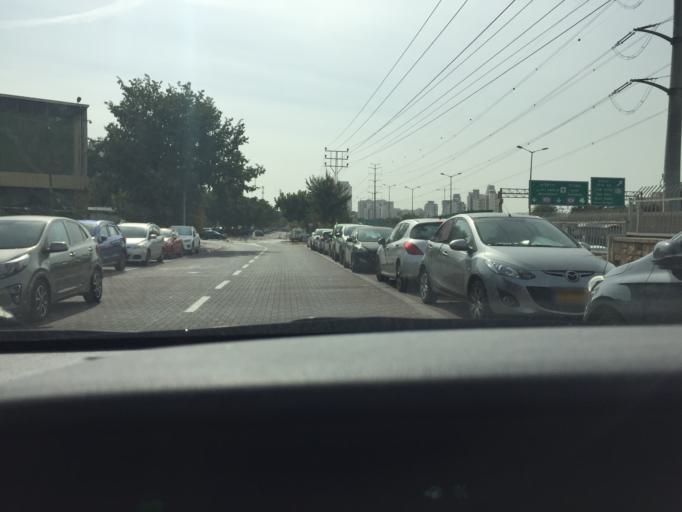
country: IL
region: Tel Aviv
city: Giv`at Shemu'el
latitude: 32.0705
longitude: 34.8425
